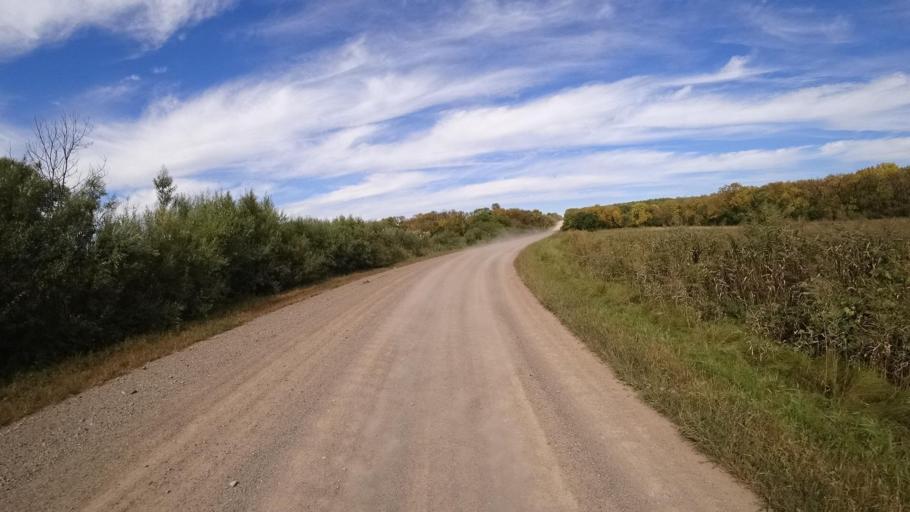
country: RU
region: Primorskiy
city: Yakovlevka
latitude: 44.6183
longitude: 133.5970
